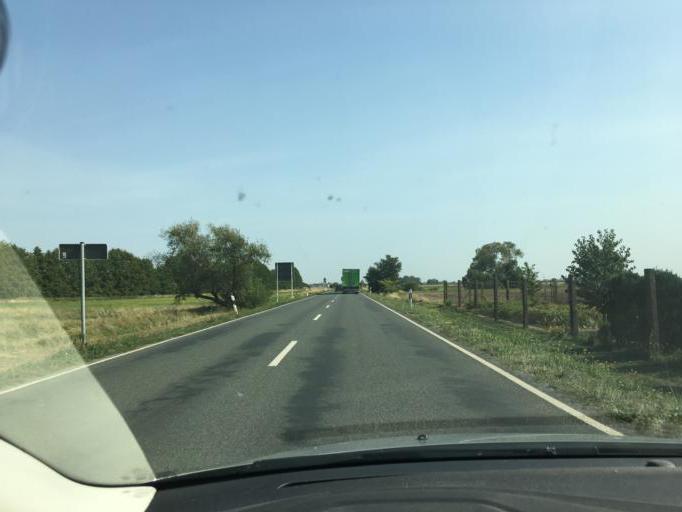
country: DE
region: Saxony-Anhalt
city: Plotzky
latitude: 52.0059
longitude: 11.8011
